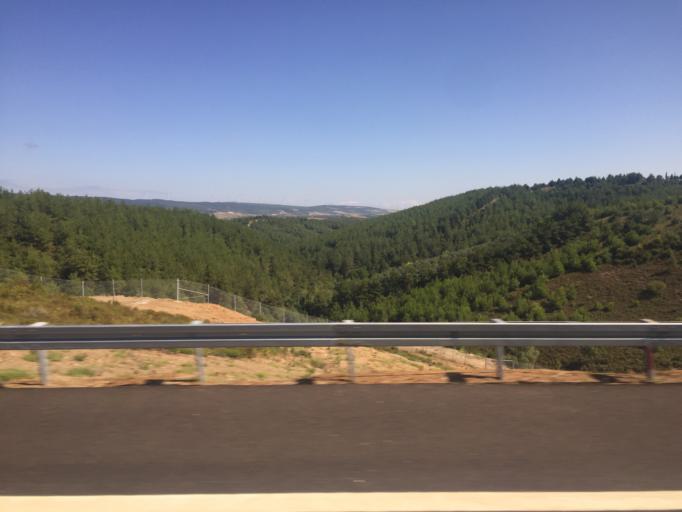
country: TR
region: Bursa
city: Mahmudiye
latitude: 40.2767
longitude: 28.5443
